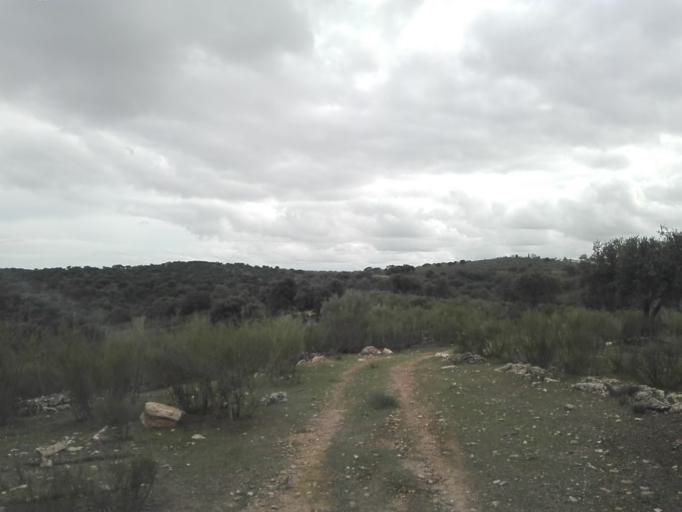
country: ES
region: Extremadura
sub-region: Provincia de Badajoz
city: Hinojosa del Valle
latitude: 38.4407
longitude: -6.1945
